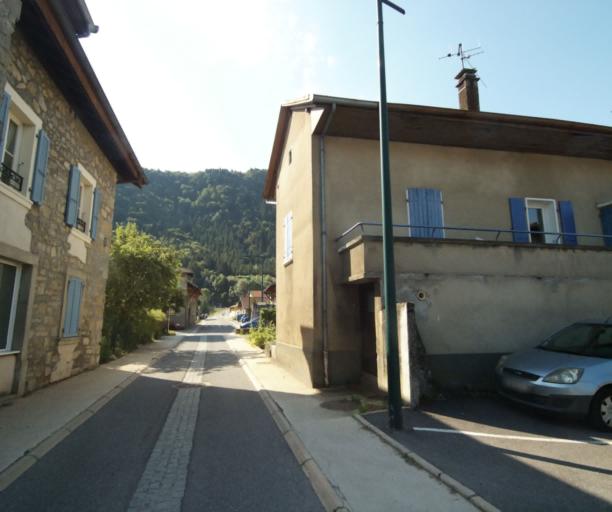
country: FR
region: Rhone-Alpes
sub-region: Departement de la Haute-Savoie
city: Allinges
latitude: 46.3124
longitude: 6.4913
